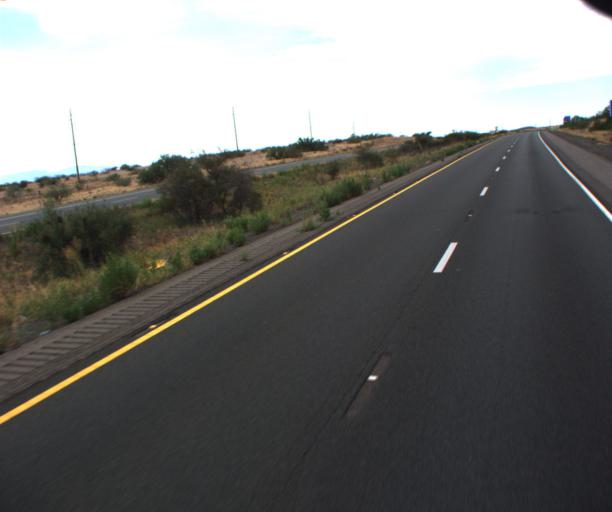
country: US
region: Arizona
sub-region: Yavapai County
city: Spring Valley
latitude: 34.3483
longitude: -112.1176
